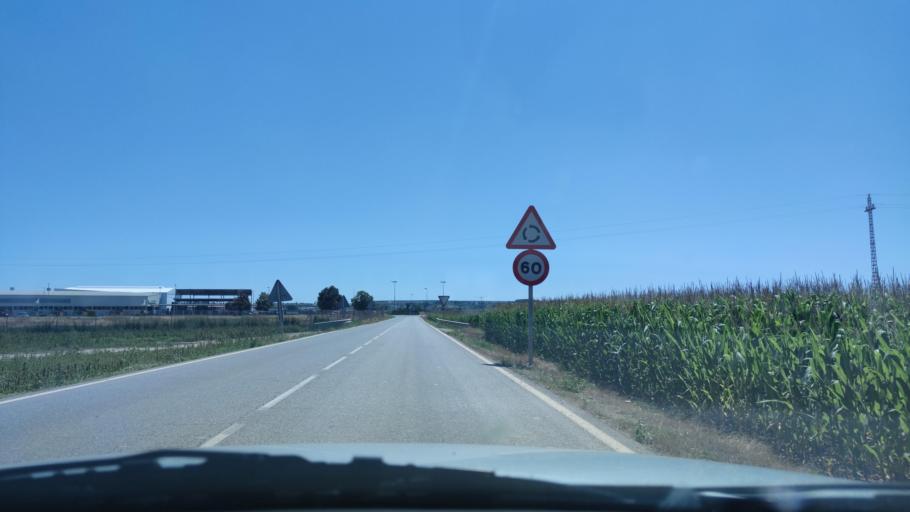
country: ES
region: Catalonia
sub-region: Provincia de Lleida
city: Mollerussa
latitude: 41.6314
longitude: 0.8767
